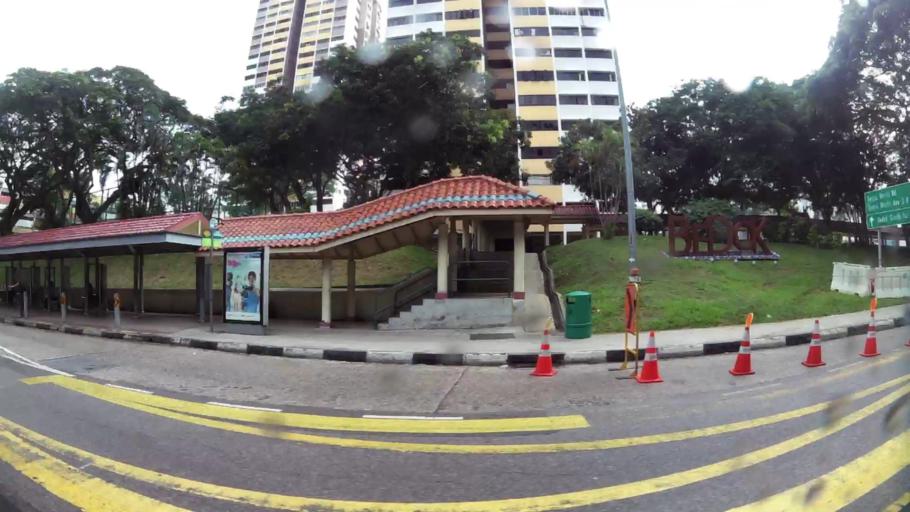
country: SG
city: Singapore
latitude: 1.3255
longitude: 103.9420
